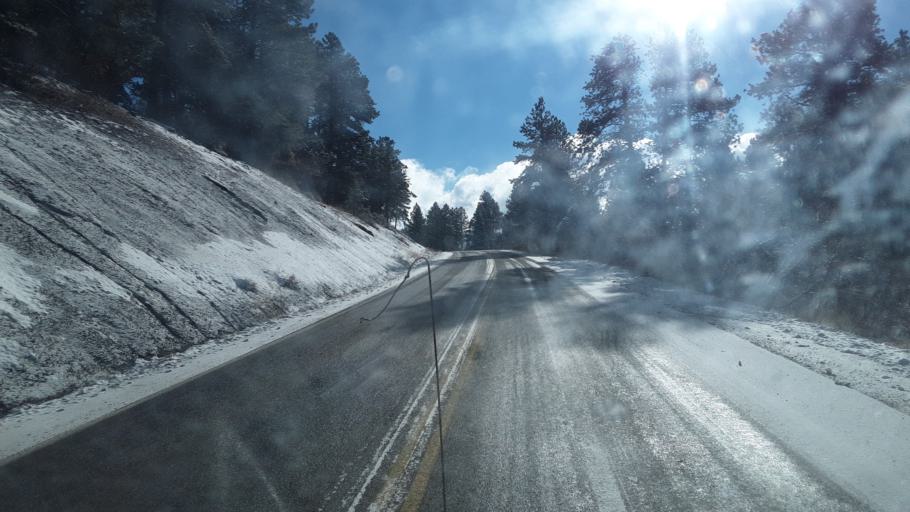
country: US
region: Colorado
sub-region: La Plata County
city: Durango
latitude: 37.3121
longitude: -107.7990
